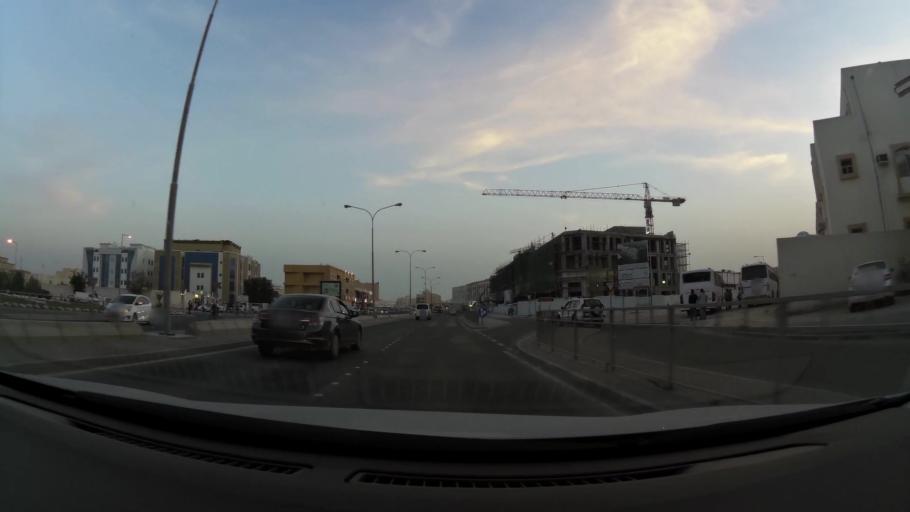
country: QA
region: Al Wakrah
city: Al Wakrah
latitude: 25.1667
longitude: 51.5977
